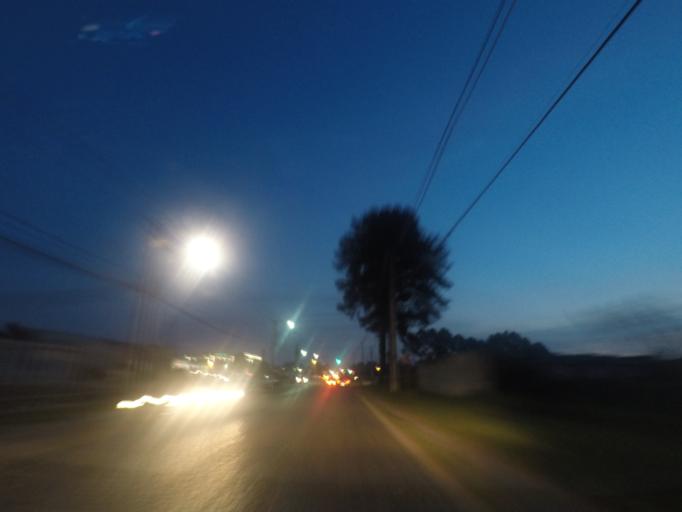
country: BR
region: Parana
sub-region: Pinhais
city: Pinhais
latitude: -25.4905
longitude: -49.1579
